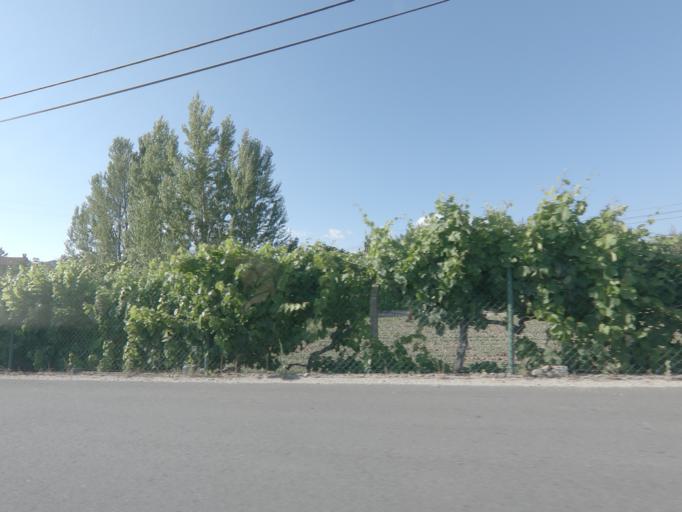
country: PT
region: Vila Real
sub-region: Chaves
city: Chaves
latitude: 41.7921
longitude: -7.4252
